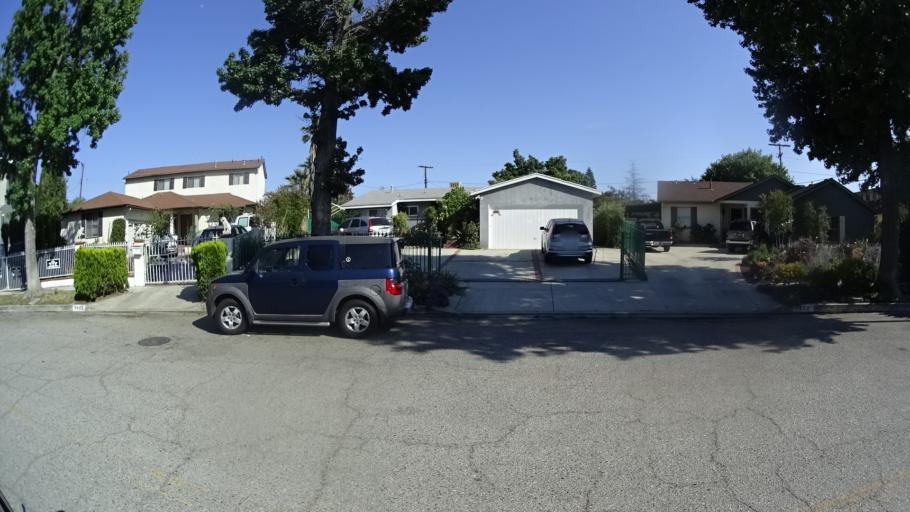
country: US
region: California
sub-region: Los Angeles County
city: Van Nuys
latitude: 34.2129
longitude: -118.4260
